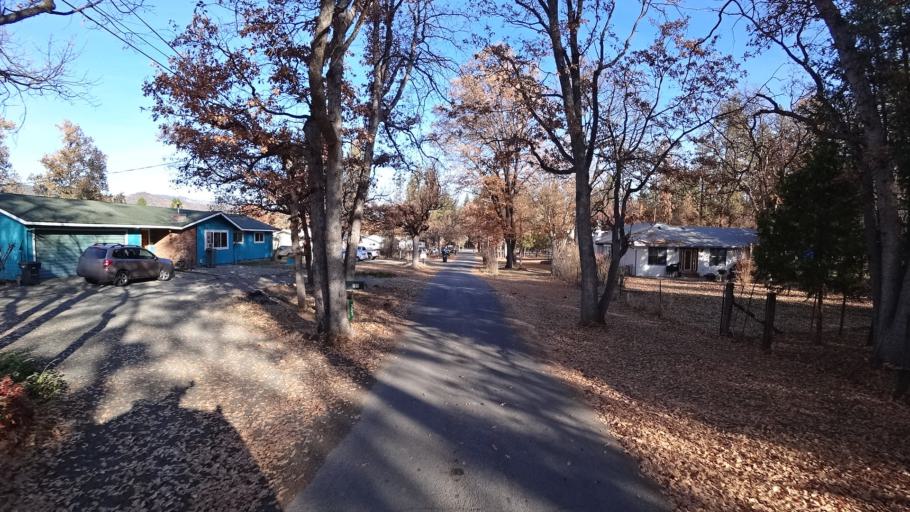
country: US
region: California
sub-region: Siskiyou County
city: Yreka
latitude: 41.6855
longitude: -122.6412
